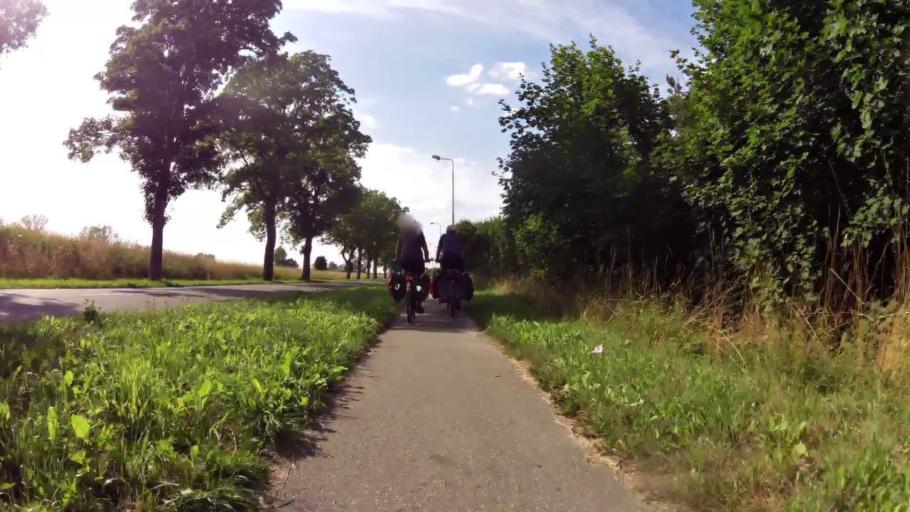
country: PL
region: West Pomeranian Voivodeship
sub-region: Powiat lobeski
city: Wegorzyno
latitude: 53.5490
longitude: 15.5452
